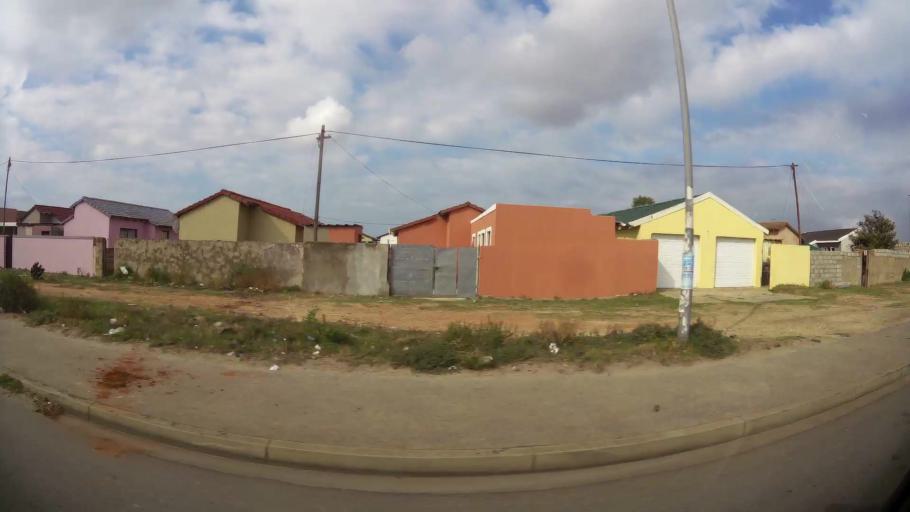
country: ZA
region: Eastern Cape
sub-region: Nelson Mandela Bay Metropolitan Municipality
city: Port Elizabeth
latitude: -33.8114
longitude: 25.6003
